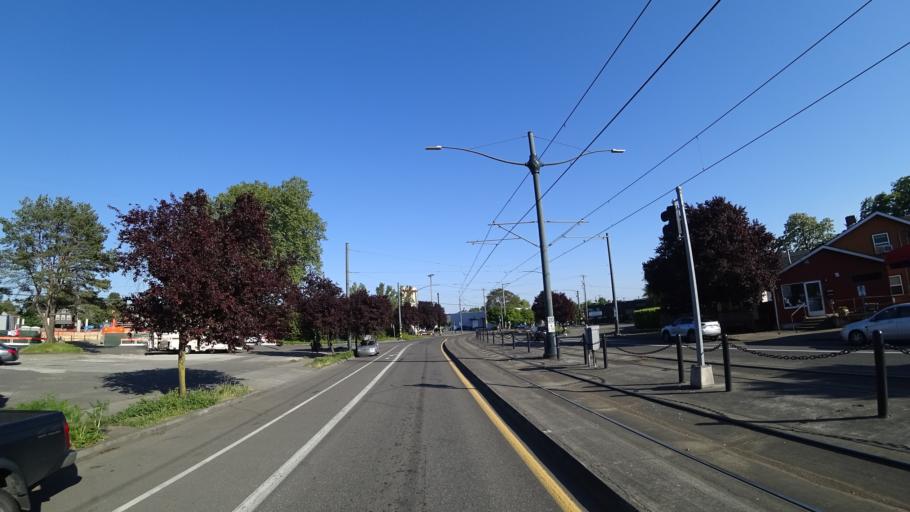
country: US
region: Oregon
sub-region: Multnomah County
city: Portland
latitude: 45.5542
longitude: -122.6817
